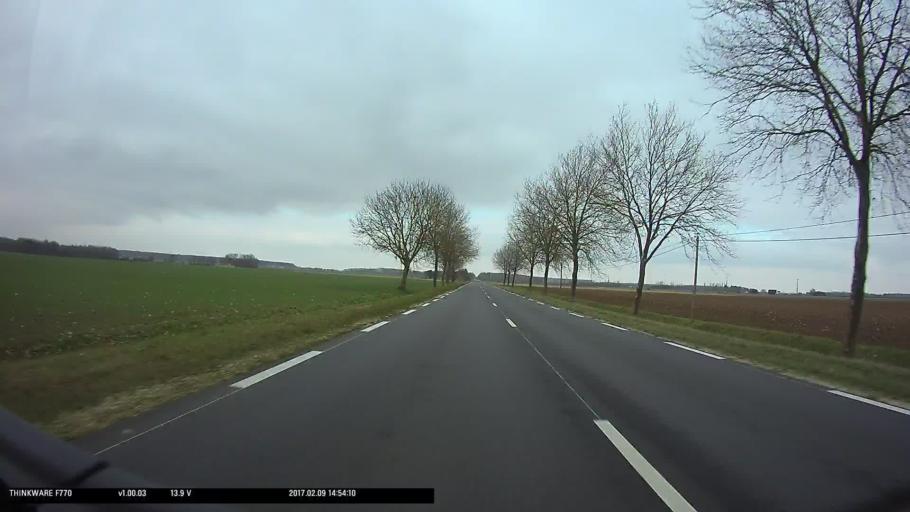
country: FR
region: Centre
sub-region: Departement du Cher
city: Levet
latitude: 46.8967
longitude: 2.4143
